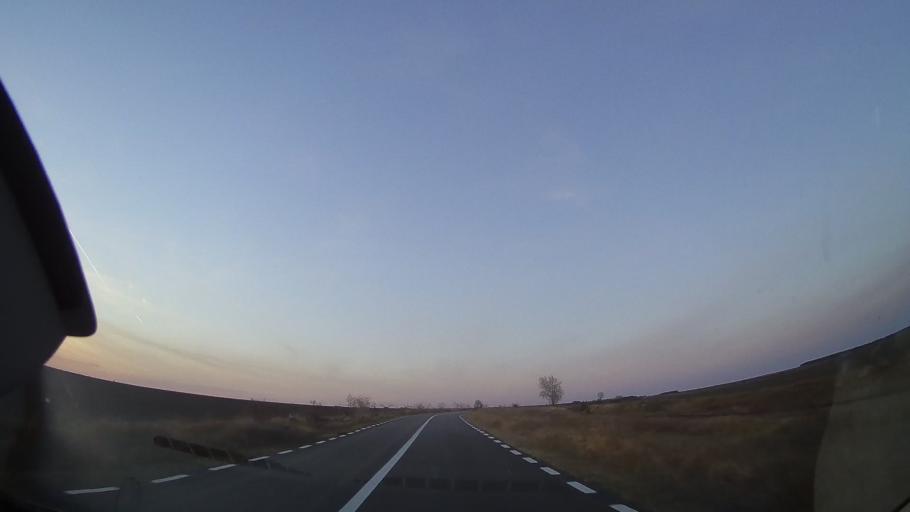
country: RO
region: Constanta
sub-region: Comuna Cobadin
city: Cobadin
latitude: 44.0259
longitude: 28.2644
